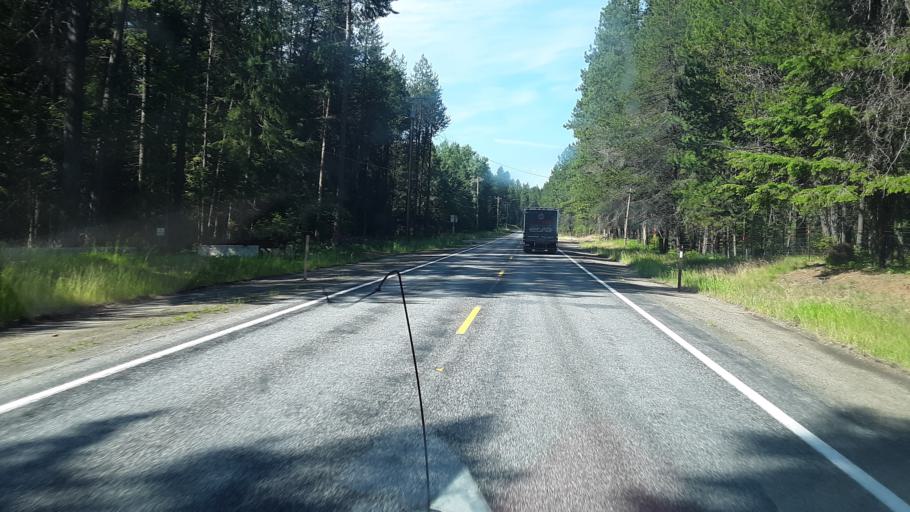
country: US
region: Idaho
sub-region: Boundary County
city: Bonners Ferry
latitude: 48.5305
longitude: -116.4282
